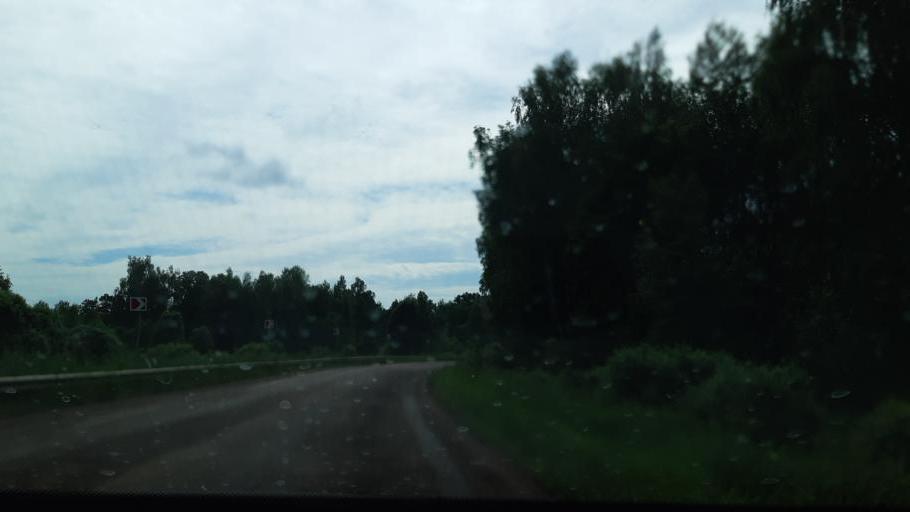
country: RU
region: Moskovskaya
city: Vereya
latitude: 55.3113
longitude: 36.1196
